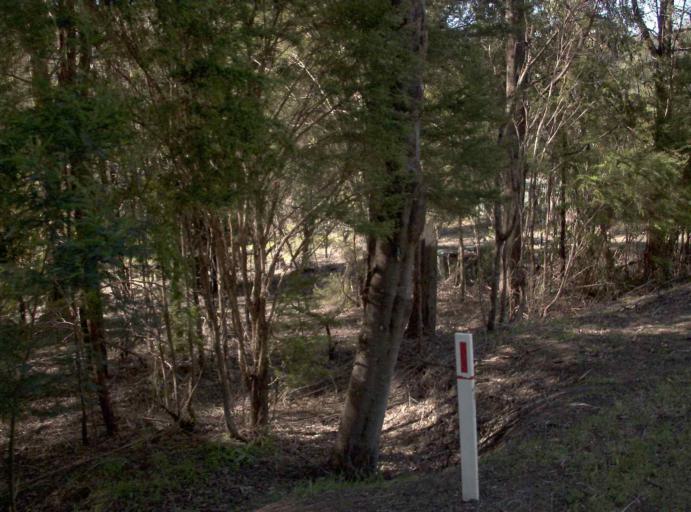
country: AU
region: Victoria
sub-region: Baw Baw
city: Warragul
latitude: -37.8900
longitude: 145.9303
